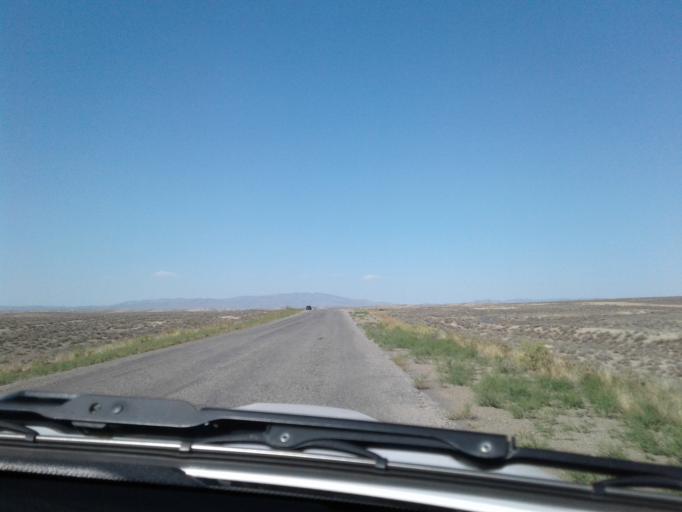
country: TM
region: Balkan
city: Magtymguly
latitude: 38.6150
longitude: 56.2214
